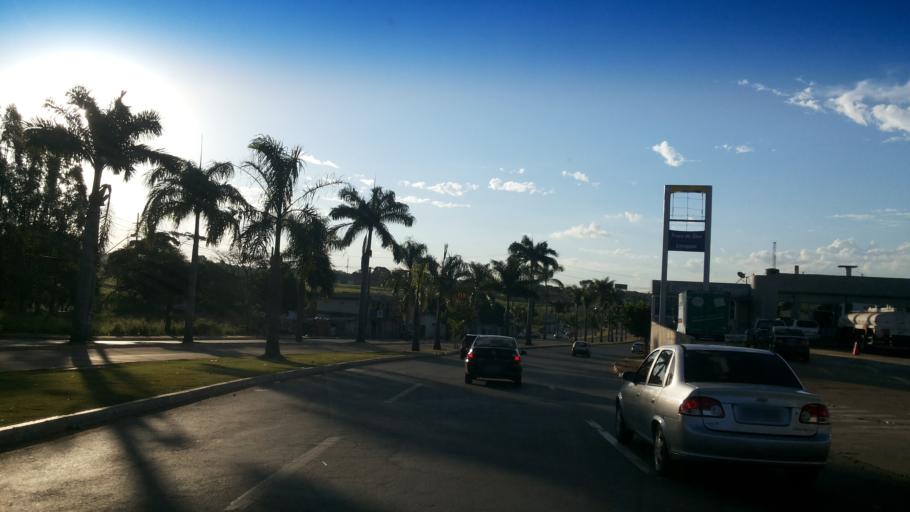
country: BR
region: Goias
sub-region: Goiania
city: Goiania
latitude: -16.6569
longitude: -49.2621
